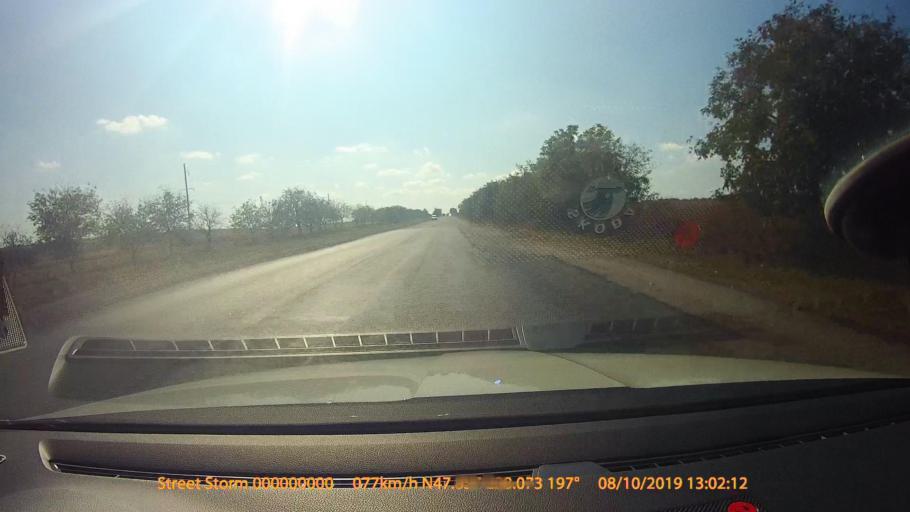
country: MD
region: Singerei
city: Biruinta
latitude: 47.8565
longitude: 28.0721
